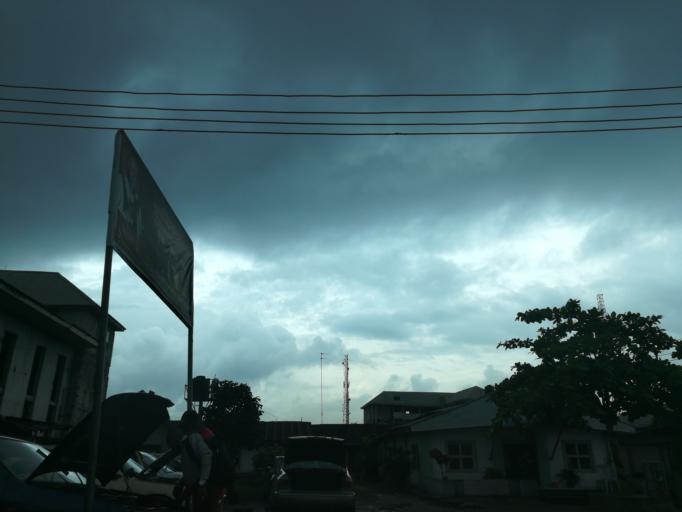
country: NG
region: Rivers
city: Port Harcourt
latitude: 4.8206
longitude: 7.0188
